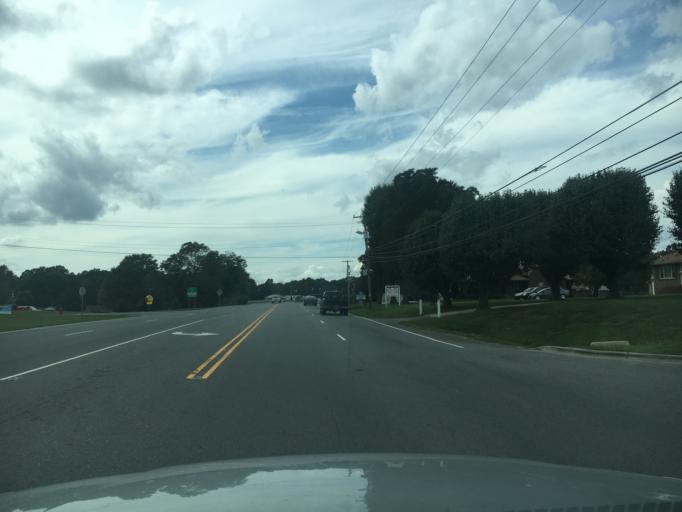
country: US
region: North Carolina
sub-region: Gaston County
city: Dallas
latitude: 35.3155
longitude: -81.1969
